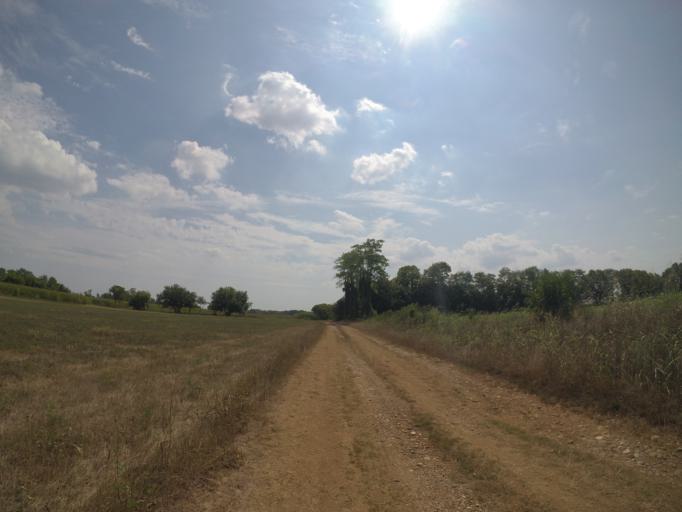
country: IT
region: Friuli Venezia Giulia
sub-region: Provincia di Udine
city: Bertiolo
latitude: 45.9562
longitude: 13.0703
